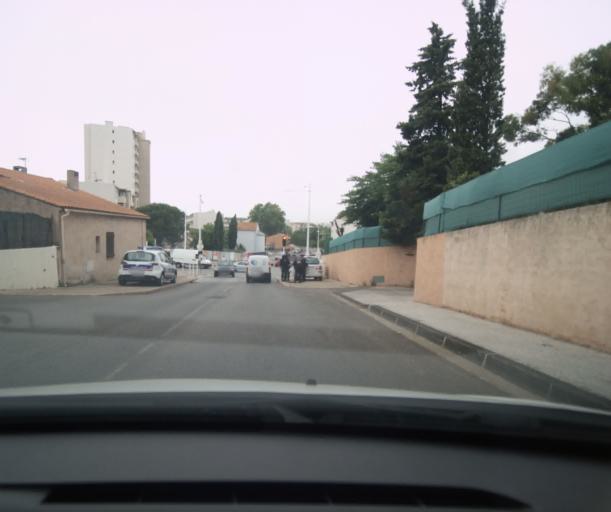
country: FR
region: Provence-Alpes-Cote d'Azur
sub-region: Departement du Var
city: La Valette-du-Var
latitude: 43.1223
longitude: 5.9822
